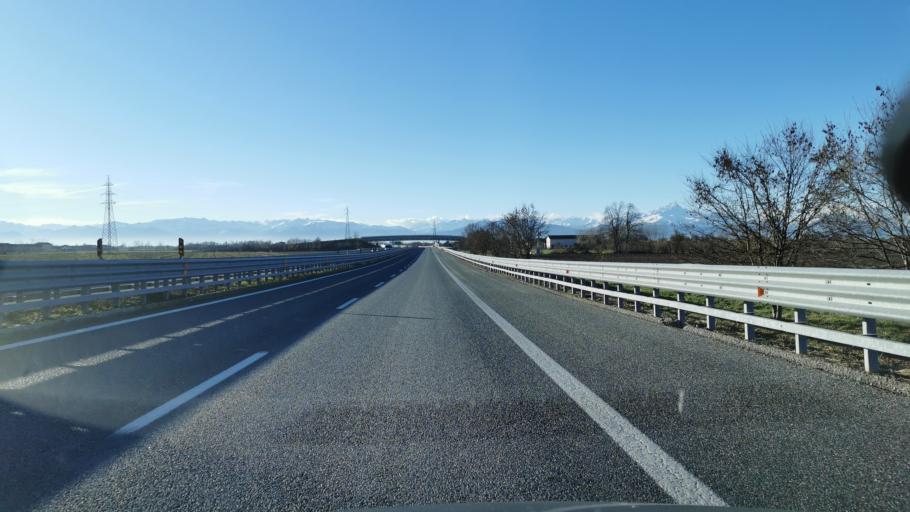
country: IT
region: Piedmont
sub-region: Provincia di Cuneo
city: Trinita
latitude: 44.4701
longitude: 7.7461
